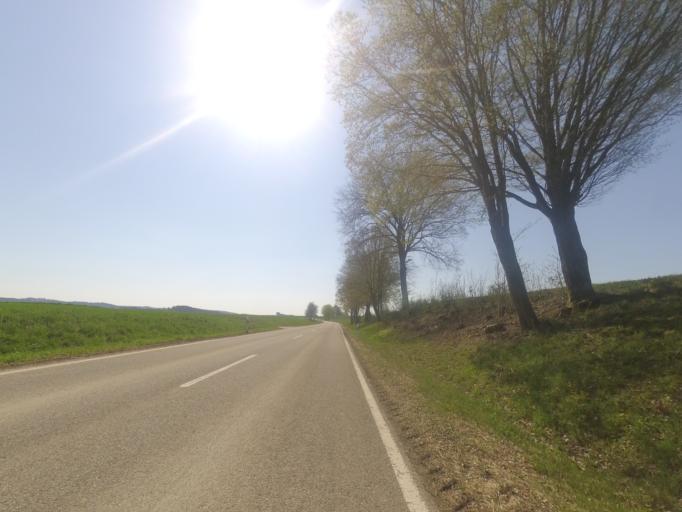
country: DE
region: Bavaria
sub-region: Swabia
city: Pfaffenhofen an der Roth
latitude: 48.3535
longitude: 10.1927
